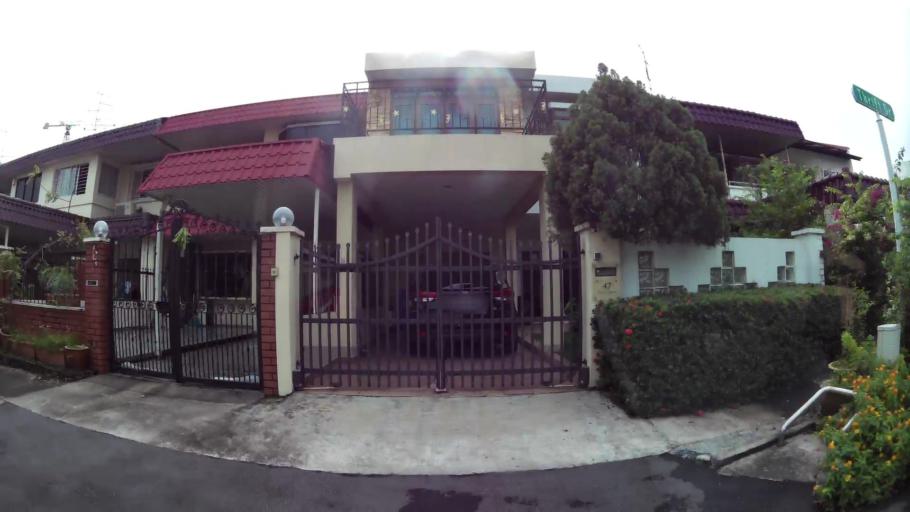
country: SG
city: Singapore
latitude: 1.3447
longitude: 103.8830
